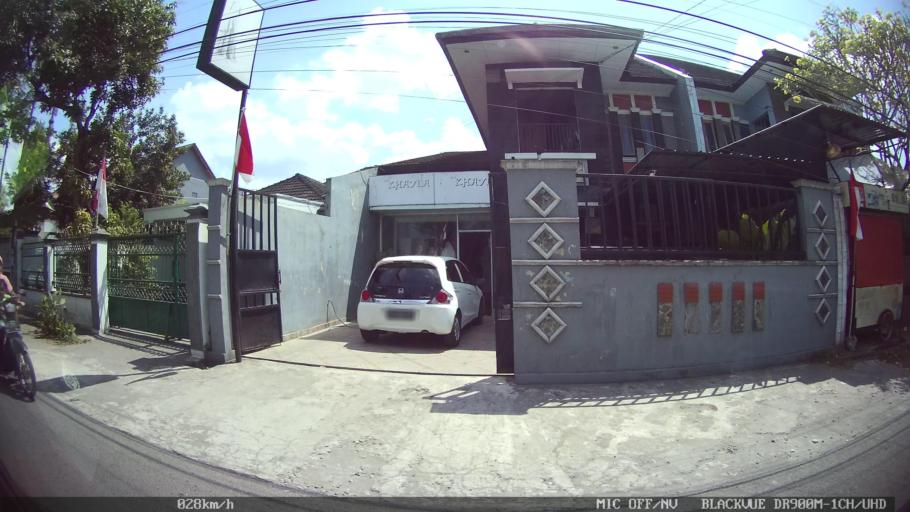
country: ID
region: Daerah Istimewa Yogyakarta
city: Sewon
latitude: -7.8433
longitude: 110.3890
